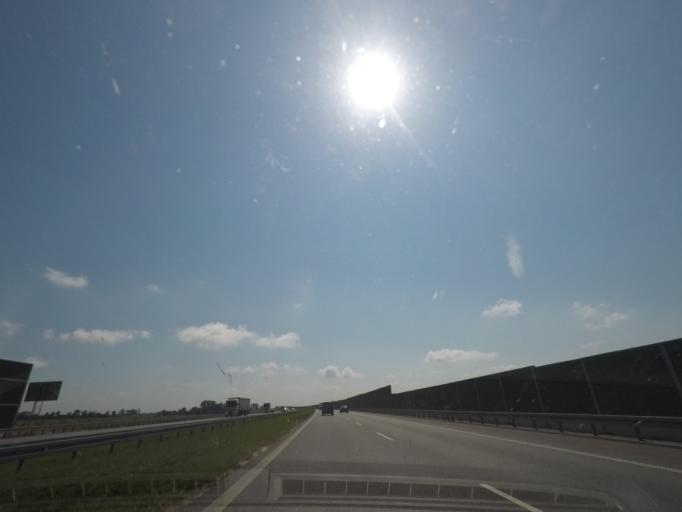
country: PL
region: Kujawsko-Pomorskie
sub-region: Powiat wloclawski
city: Czerniewice
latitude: 52.5323
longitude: 19.0711
